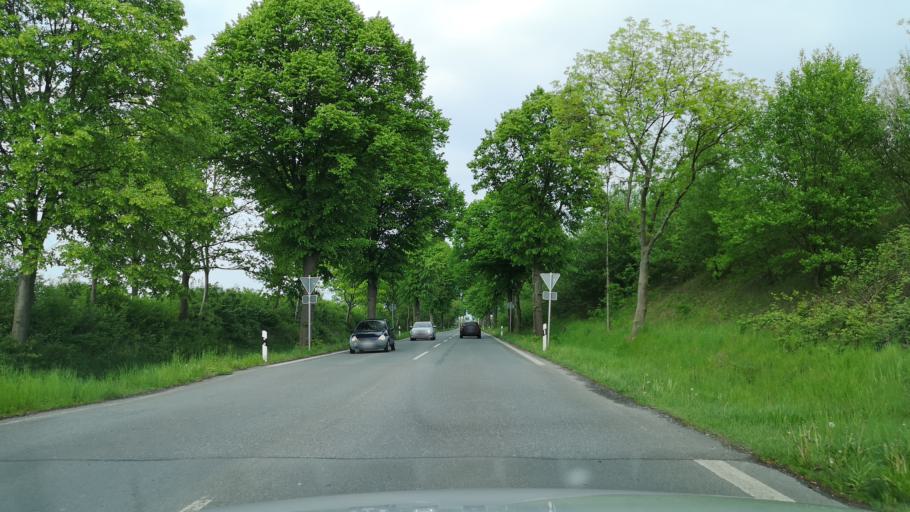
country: DE
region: North Rhine-Westphalia
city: Iserlohn
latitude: 51.4229
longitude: 7.7162
